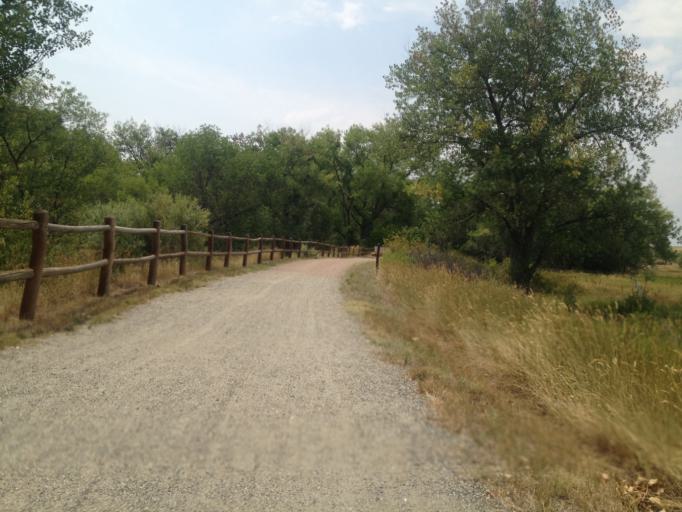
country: US
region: Colorado
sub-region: Boulder County
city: Superior
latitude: 39.9483
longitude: -105.1741
